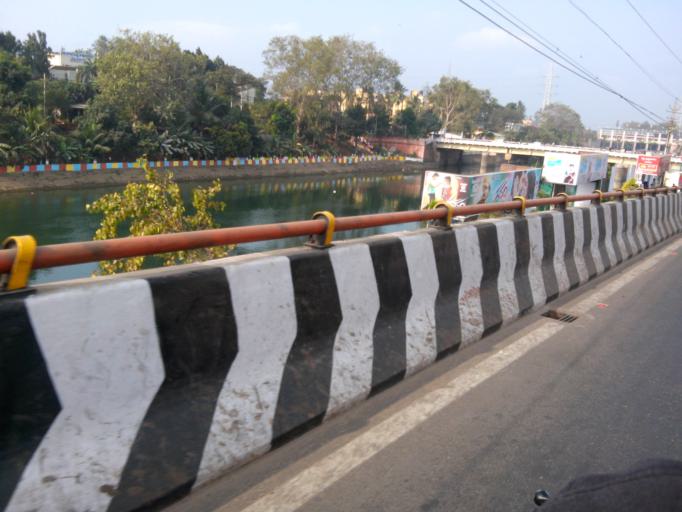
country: IN
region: Andhra Pradesh
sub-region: Krishna
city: Vijayawada
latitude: 16.5119
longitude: 80.6127
